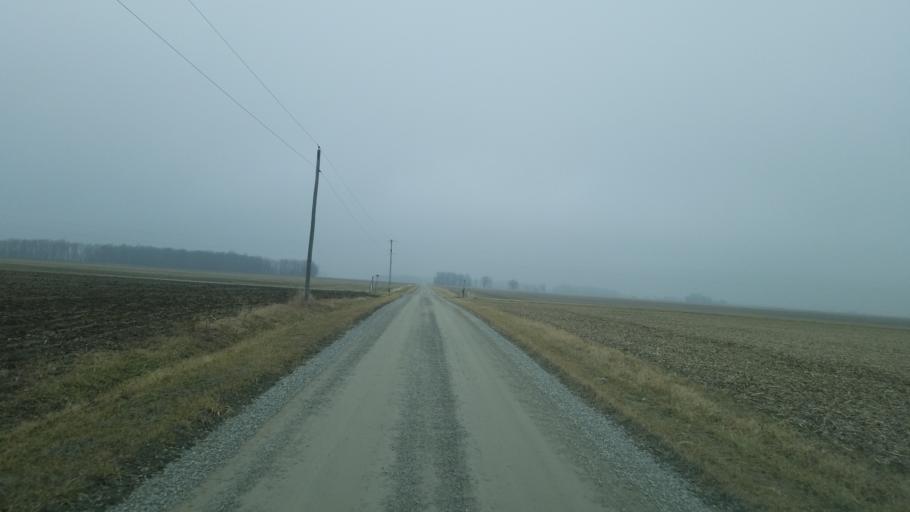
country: US
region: Indiana
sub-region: Adams County
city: Geneva
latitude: 40.6250
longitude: -85.0697
